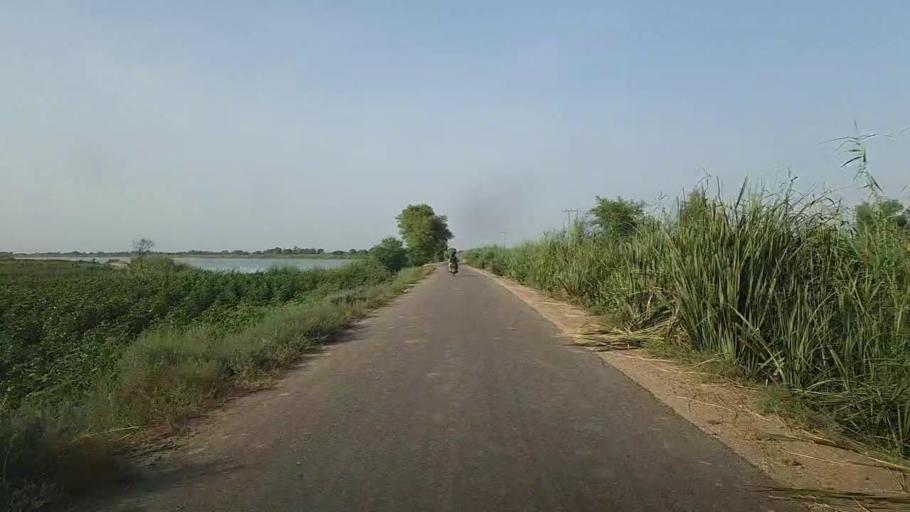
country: PK
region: Sindh
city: Khairpur
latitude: 28.0784
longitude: 69.8130
